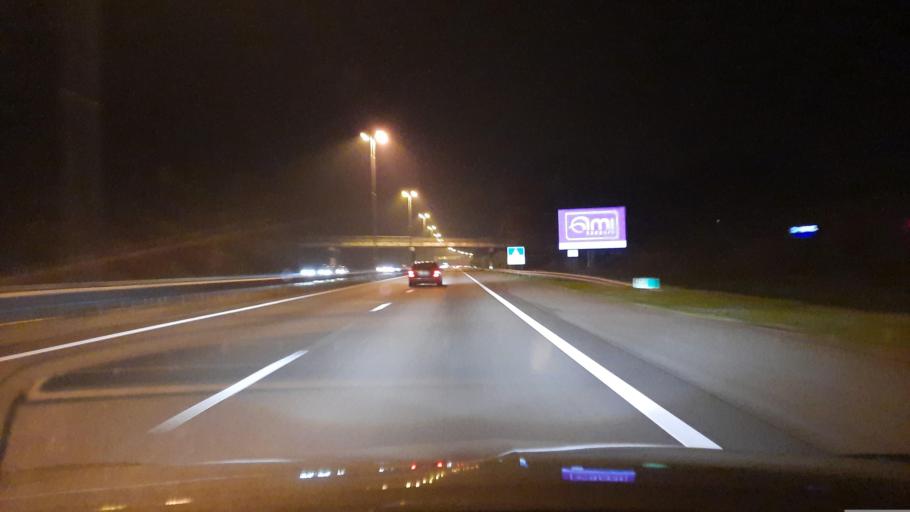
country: NL
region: Gelderland
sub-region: Gemeente Barneveld
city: Terschuur
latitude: 52.1631
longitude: 5.5249
